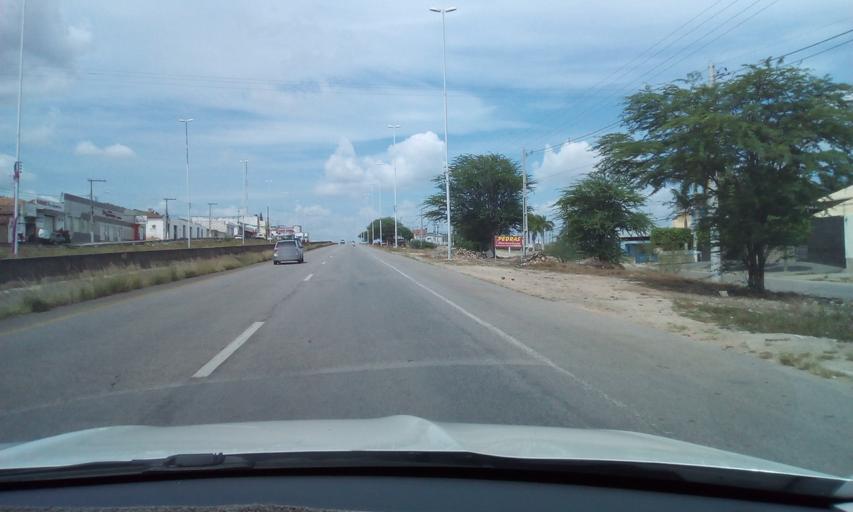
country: BR
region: Pernambuco
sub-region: Bezerros
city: Bezerros
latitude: -8.2440
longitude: -35.7538
